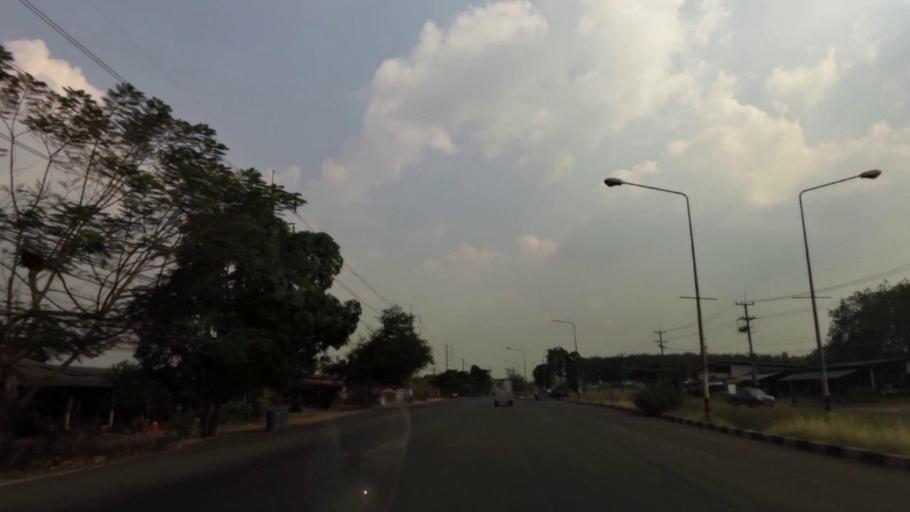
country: TH
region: Rayong
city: Wang Chan
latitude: 12.8655
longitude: 101.5902
